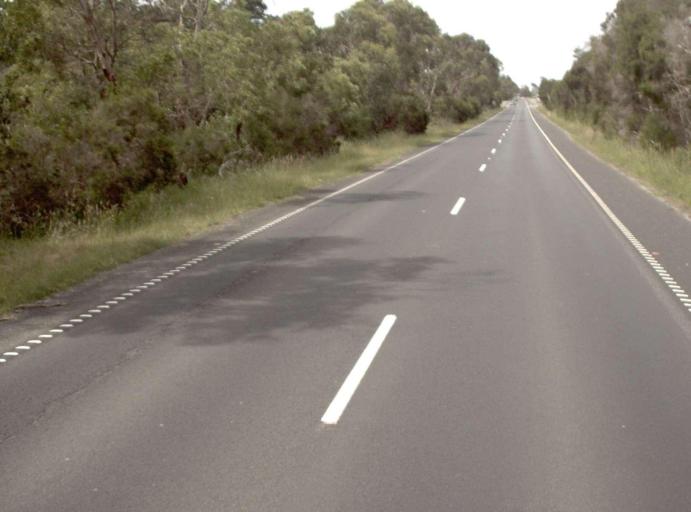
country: AU
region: Victoria
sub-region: Mornington Peninsula
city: Moorooduc
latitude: -38.2049
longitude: 145.1188
